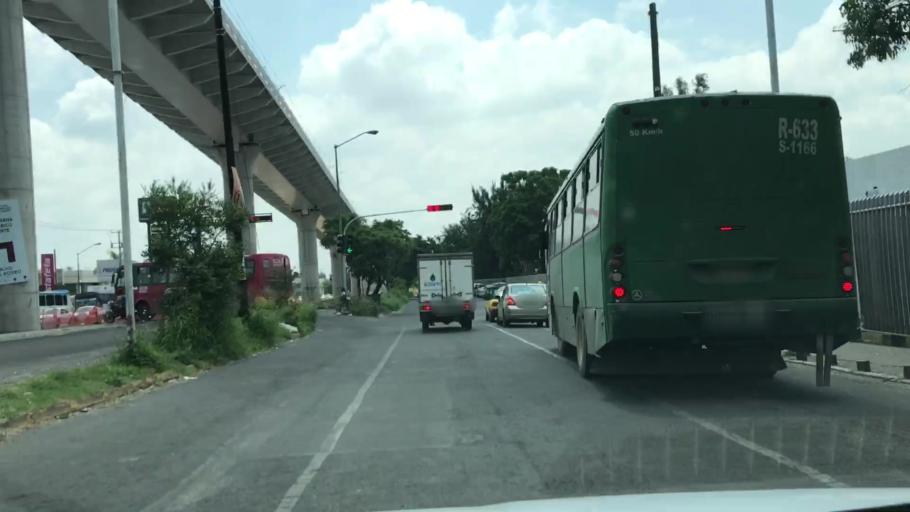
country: MX
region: Jalisco
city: Zapopan2
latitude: 20.7376
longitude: -103.4027
